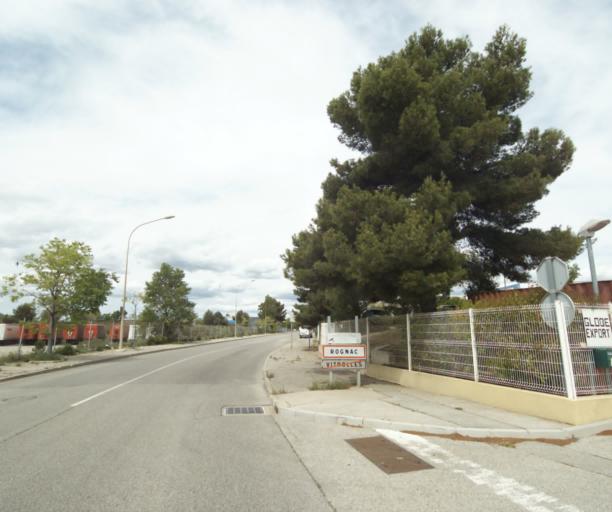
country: FR
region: Provence-Alpes-Cote d'Azur
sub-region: Departement des Bouches-du-Rhone
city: Rognac
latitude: 43.4779
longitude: 5.2339
